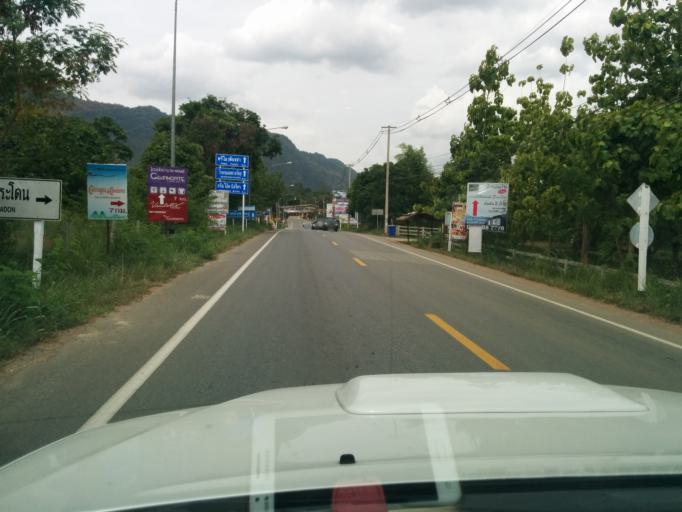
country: TH
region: Sara Buri
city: Muak Lek
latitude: 14.5893
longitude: 101.2247
